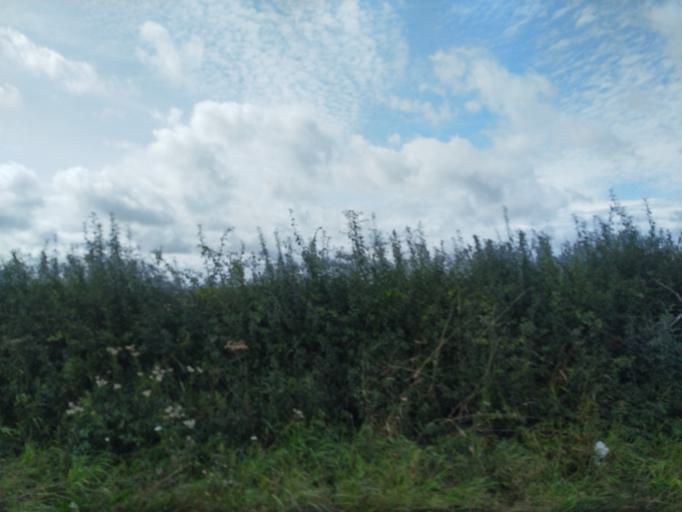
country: GB
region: England
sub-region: Dorset
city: Lytchett Matravers
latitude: 50.8067
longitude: -2.1163
